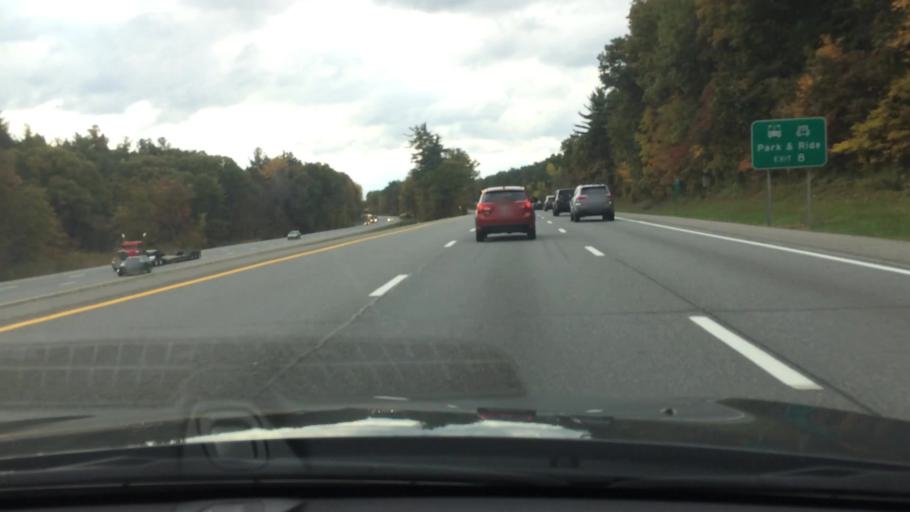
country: US
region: New York
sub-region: Albany County
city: Cohoes
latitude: 42.8310
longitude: -73.7701
